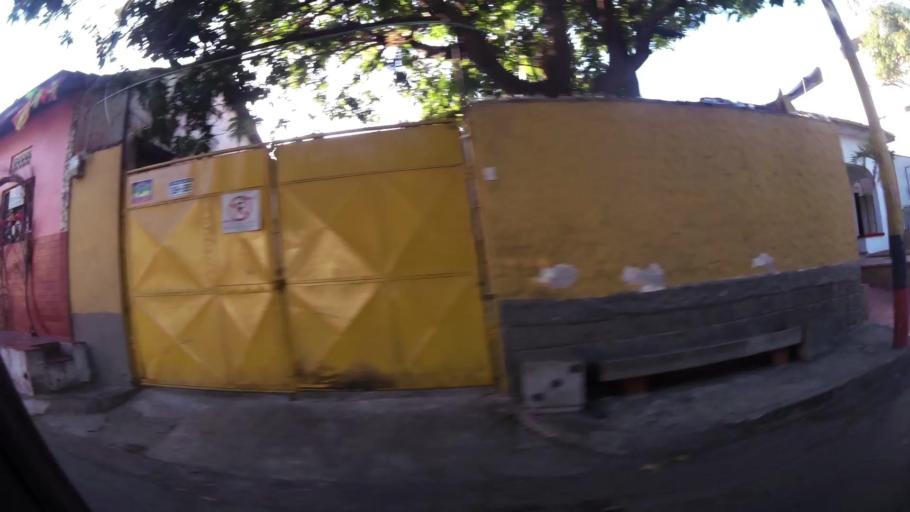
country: CO
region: Atlantico
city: Barranquilla
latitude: 10.9793
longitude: -74.7916
